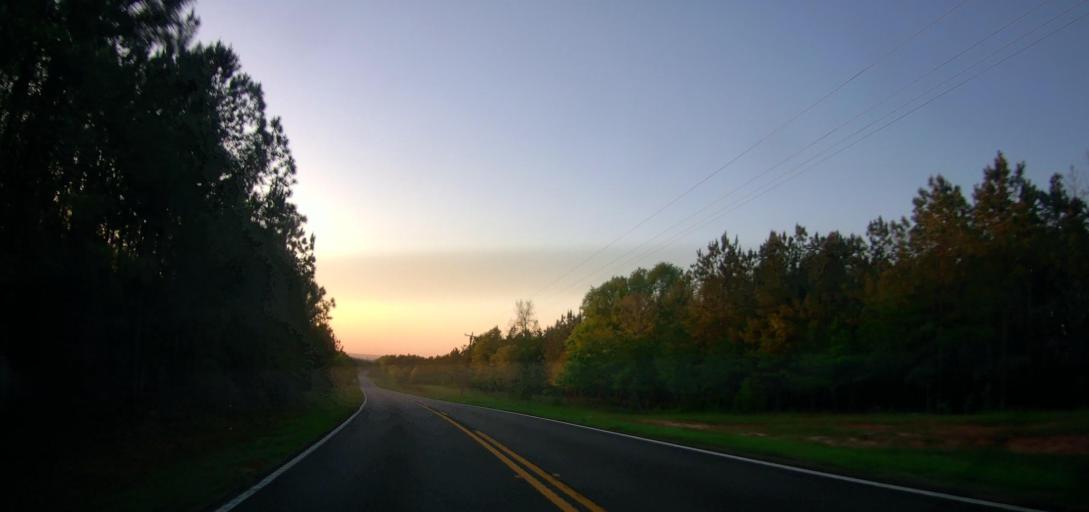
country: US
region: Georgia
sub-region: Marion County
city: Buena Vista
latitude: 32.3899
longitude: -84.5669
